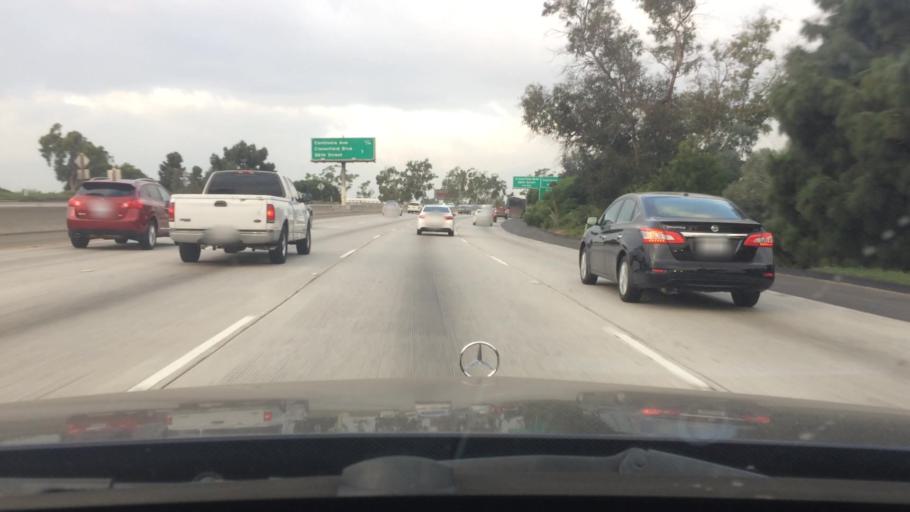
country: US
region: California
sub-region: Los Angeles County
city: Westwood, Los Angeles
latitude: 34.0281
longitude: -118.4503
